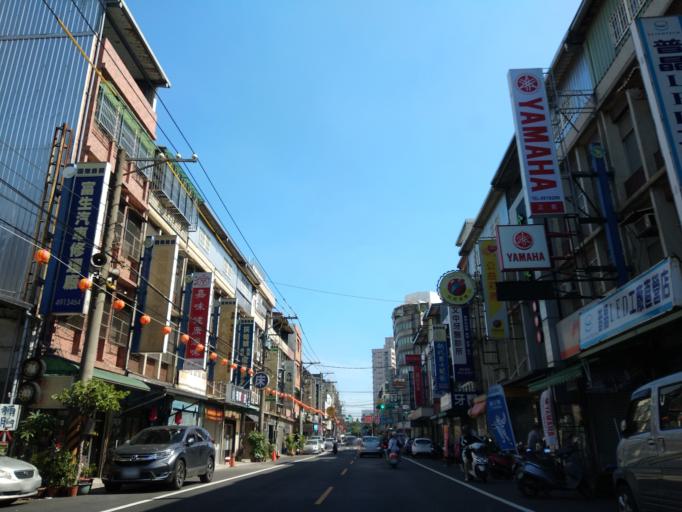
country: TW
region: Taiwan
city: Taoyuan City
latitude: 24.9466
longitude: 121.2125
